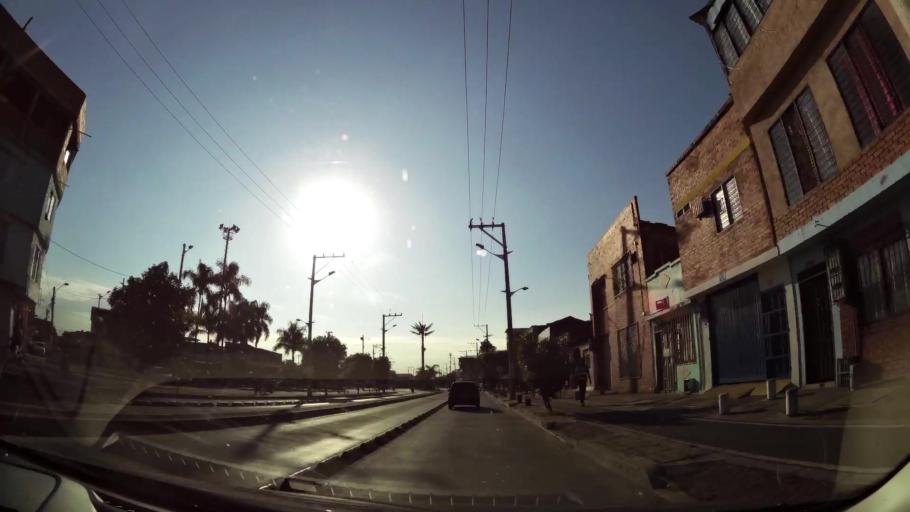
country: CO
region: Valle del Cauca
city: Cali
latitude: 3.4404
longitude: -76.5241
